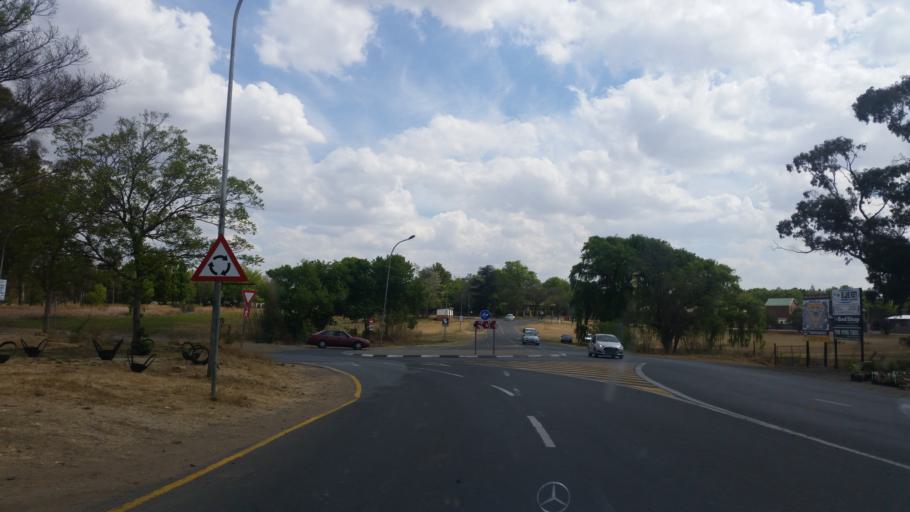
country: ZA
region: Orange Free State
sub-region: Thabo Mofutsanyana District Municipality
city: Bethlehem
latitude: -28.2394
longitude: 28.3220
